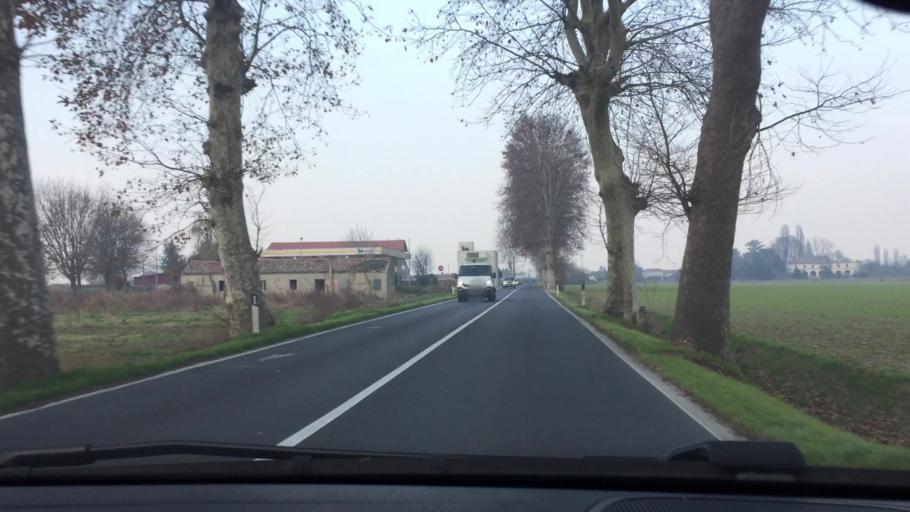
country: IT
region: Veneto
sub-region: Provincia di Venezia
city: Cavarzere
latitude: 45.1197
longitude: 12.0760
